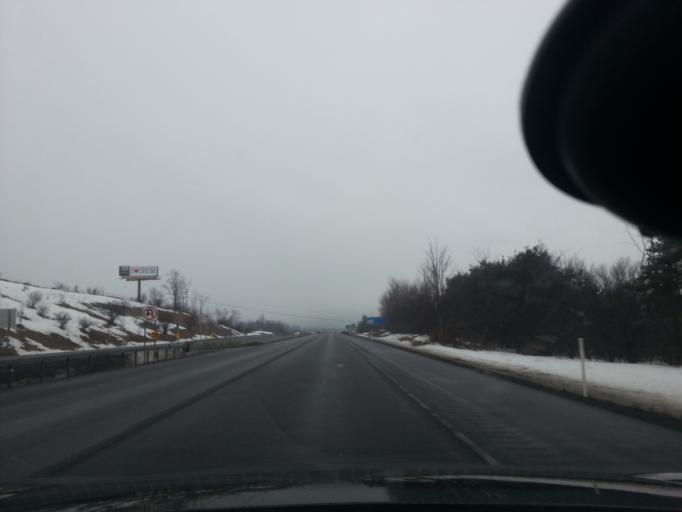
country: US
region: New York
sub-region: Jefferson County
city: Adams Center
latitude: 43.9198
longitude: -75.9745
